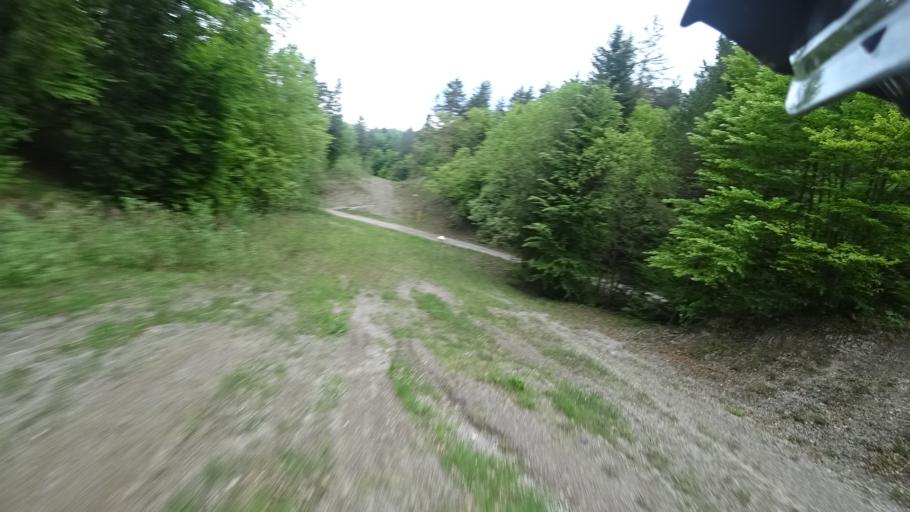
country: HR
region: Licko-Senjska
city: Jezerce
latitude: 44.8810
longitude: 15.4320
